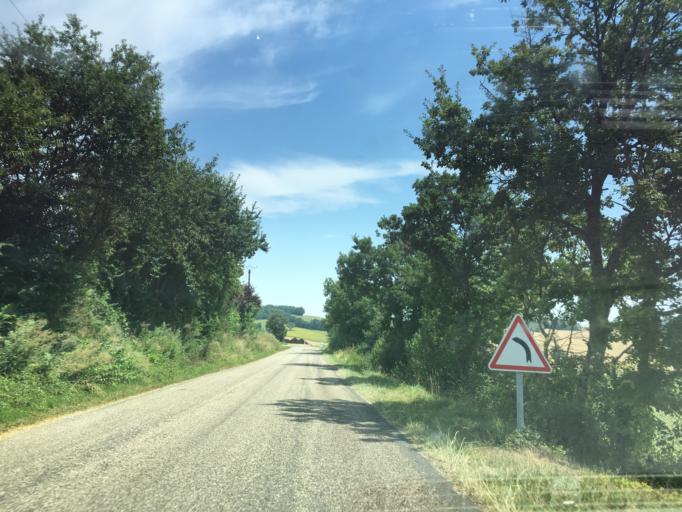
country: FR
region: Midi-Pyrenees
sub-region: Departement du Gers
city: Jegun
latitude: 43.8092
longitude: 0.5069
